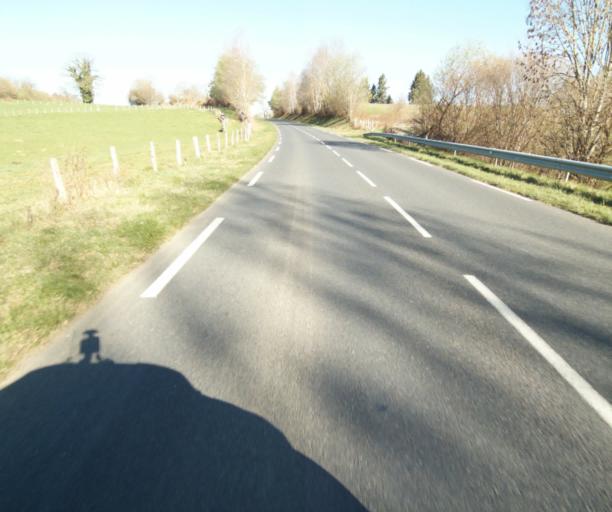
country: FR
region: Limousin
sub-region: Departement de la Correze
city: Chamboulive
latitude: 45.4074
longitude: 1.7195
